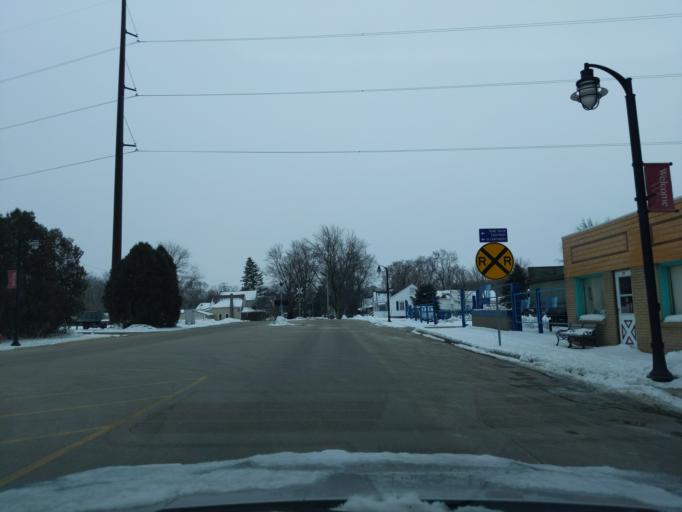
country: US
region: Indiana
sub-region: Benton County
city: Otterbein
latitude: 40.4892
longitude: -87.0963
